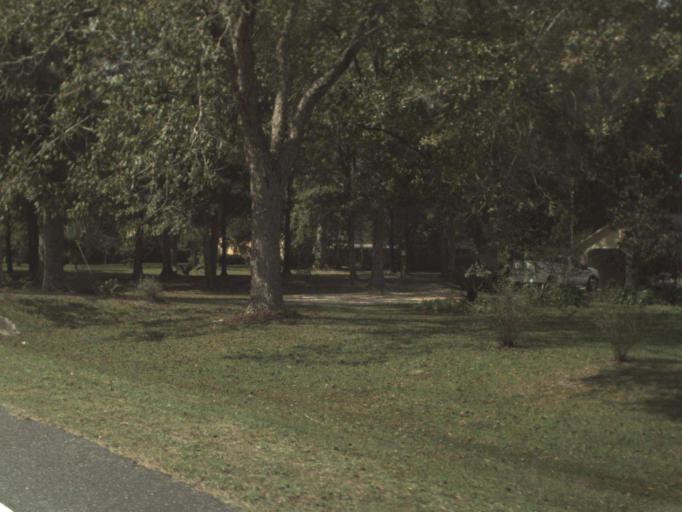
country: US
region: Florida
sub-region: Washington County
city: Chipley
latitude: 30.7956
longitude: -85.5230
